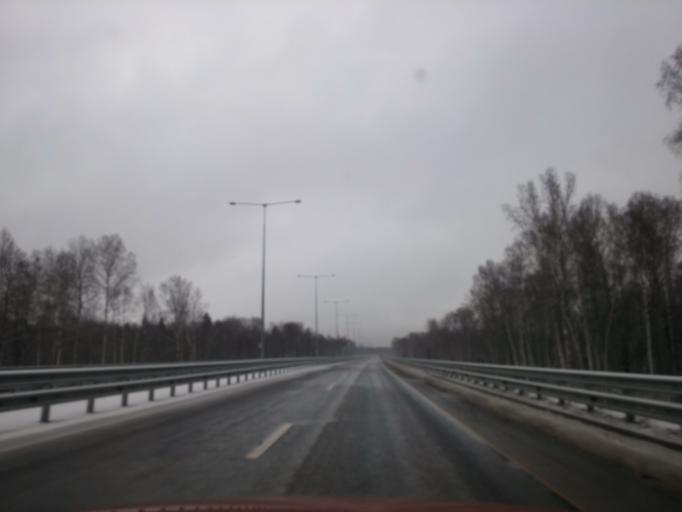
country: RU
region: Tverskaya
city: Likhoslavl'
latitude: 56.9660
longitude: 35.4699
